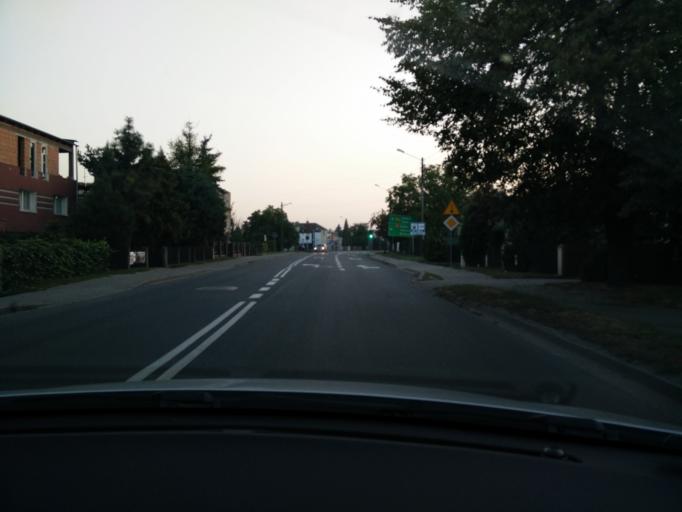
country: PL
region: Greater Poland Voivodeship
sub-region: Powiat sredzki
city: Sroda Wielkopolska
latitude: 52.2246
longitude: 17.2861
